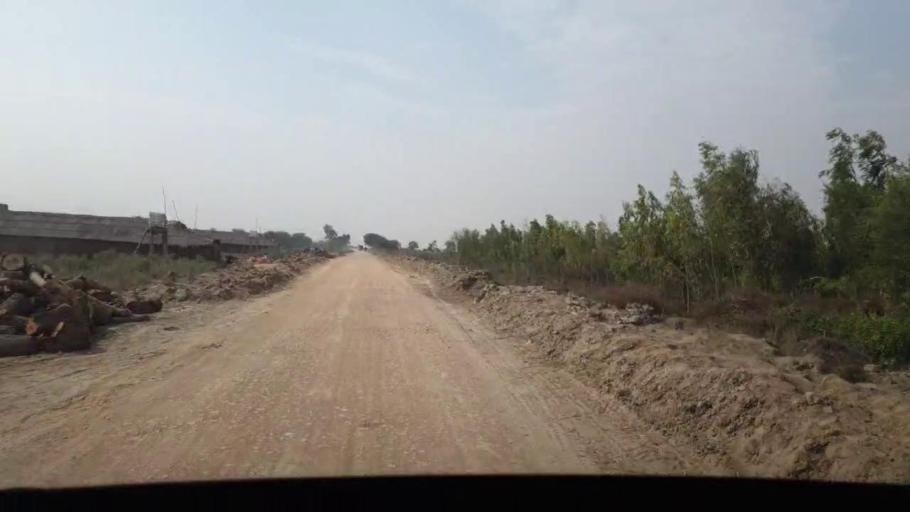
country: PK
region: Sindh
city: Chuhar Jamali
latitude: 24.3656
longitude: 67.9396
